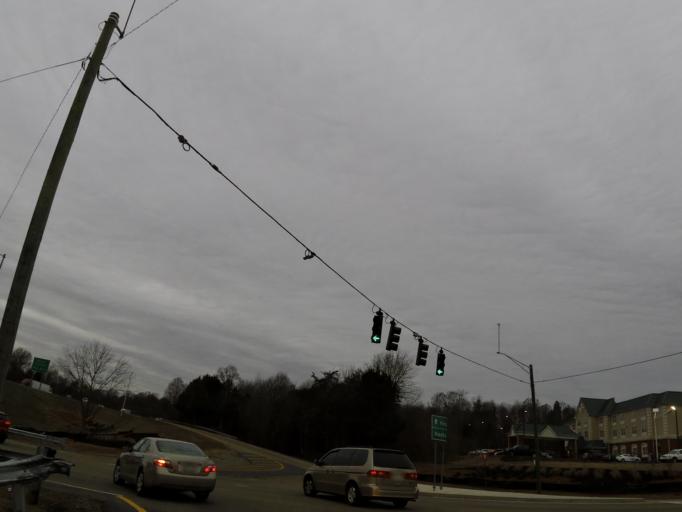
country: US
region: Tennessee
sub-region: Knox County
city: Farragut
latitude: 35.8994
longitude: -84.1748
